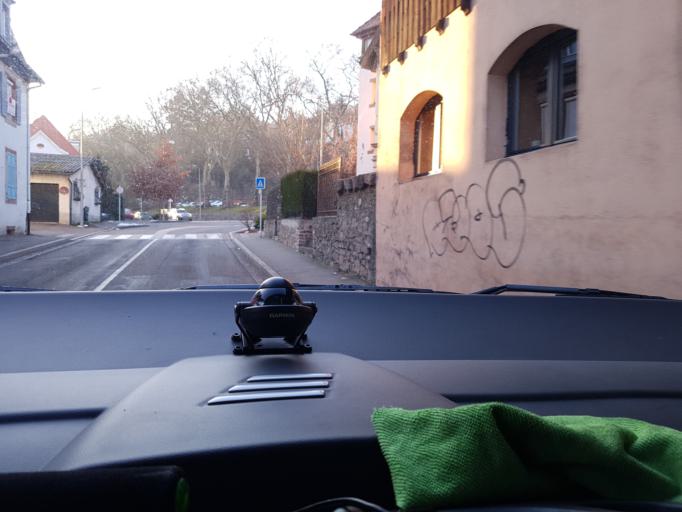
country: FR
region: Alsace
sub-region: Departement du Haut-Rhin
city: Munster
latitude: 48.0397
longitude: 7.1294
